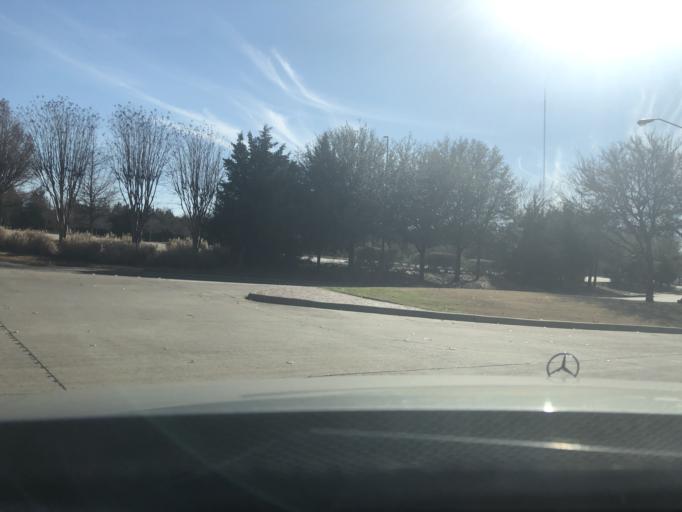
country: US
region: Texas
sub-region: Dallas County
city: Cedar Hill
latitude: 32.5925
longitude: -96.9513
